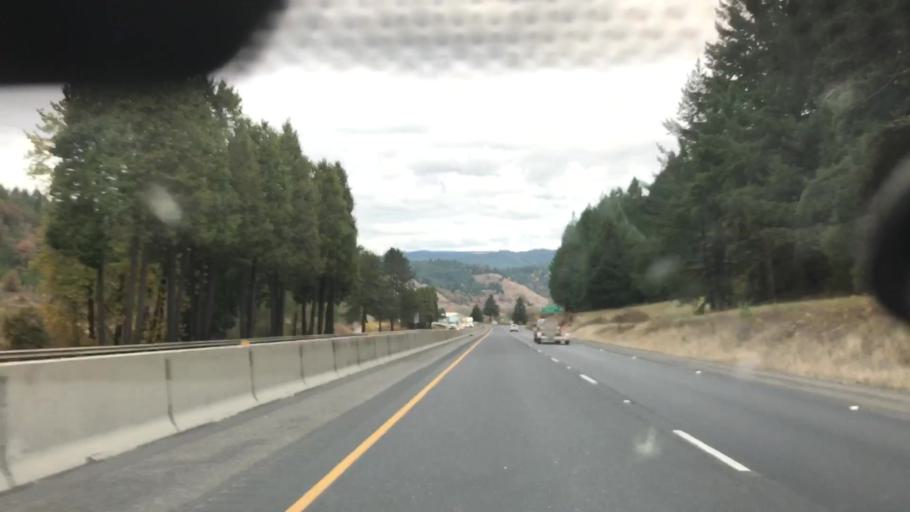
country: US
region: Oregon
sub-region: Douglas County
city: Yoncalla
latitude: 43.6039
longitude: -123.2277
